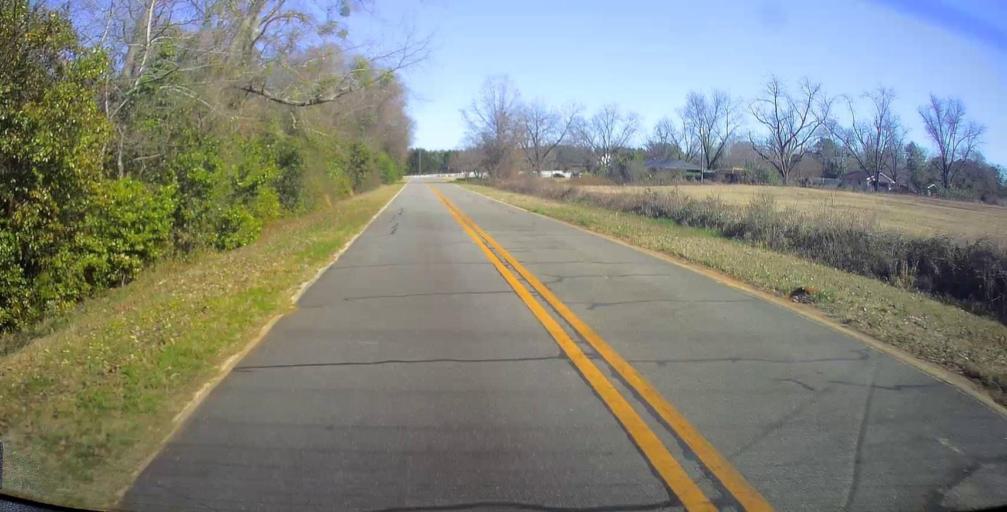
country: US
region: Georgia
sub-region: Peach County
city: Byron
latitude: 32.6235
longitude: -83.8376
